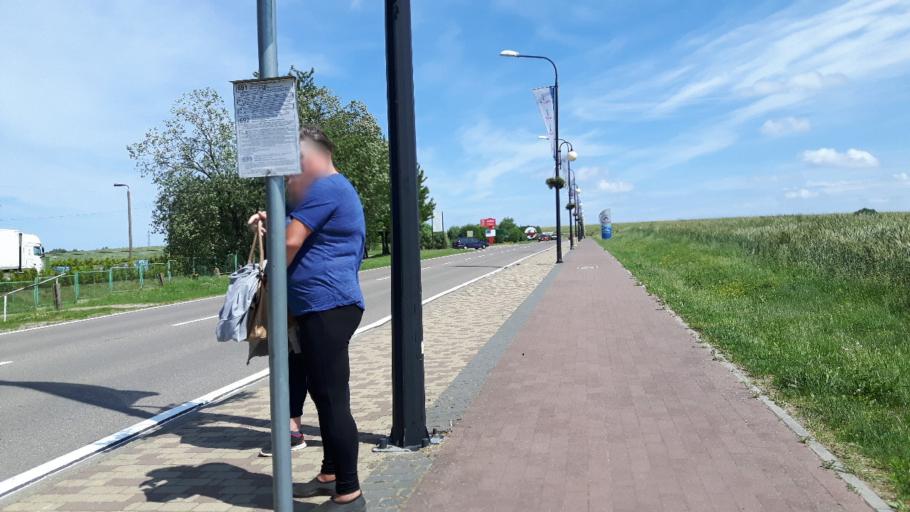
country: PL
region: Pomeranian Voivodeship
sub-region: Powiat wejherowski
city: Gniewino
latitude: 54.7151
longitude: 18.0391
